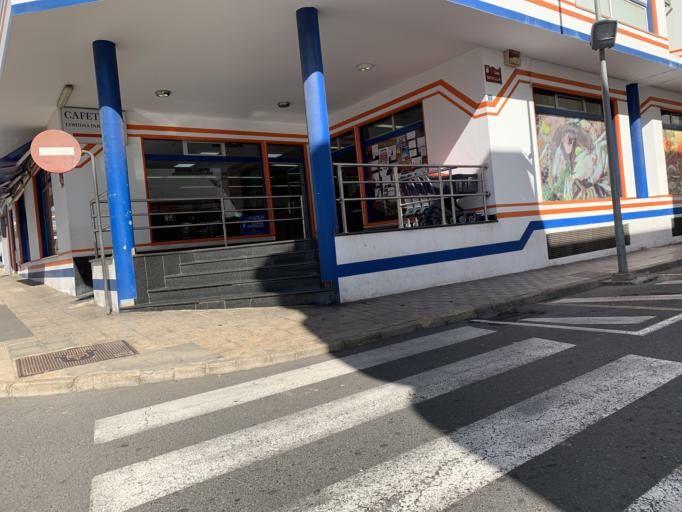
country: ES
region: Canary Islands
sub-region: Provincia de Las Palmas
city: Puerto del Rosario
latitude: 28.5021
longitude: -13.8702
